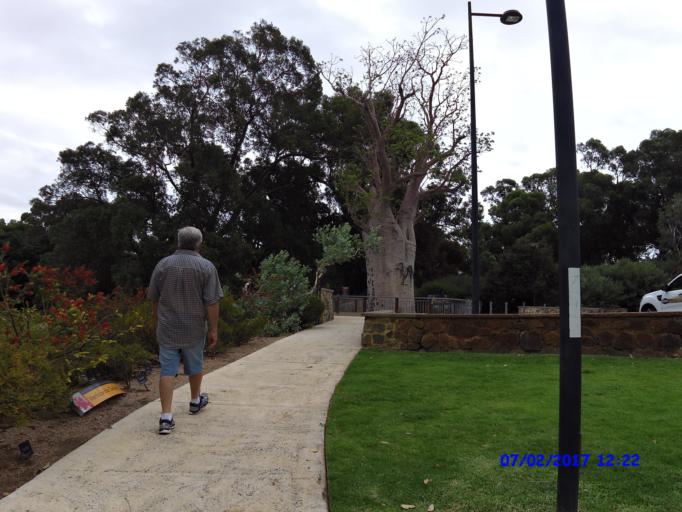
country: AU
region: Western Australia
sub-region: City of Perth
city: West Perth
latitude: -31.9622
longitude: 115.8413
